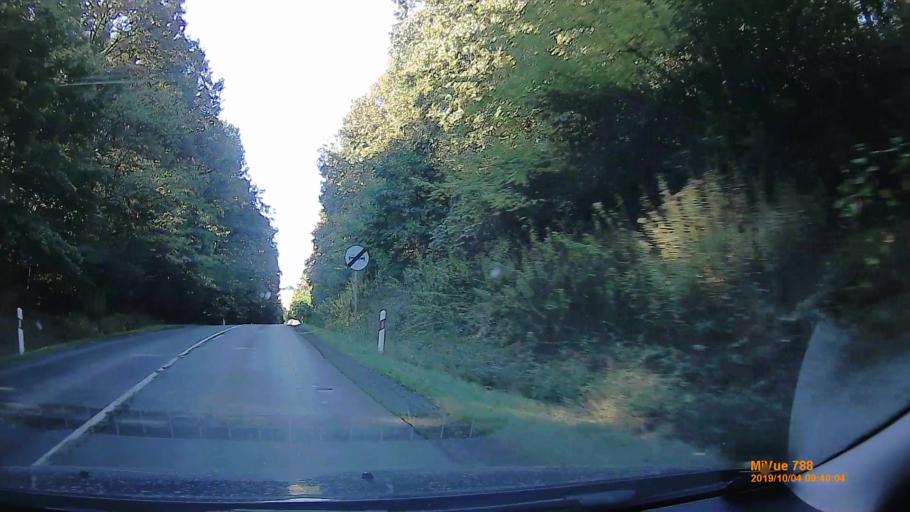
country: HU
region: Somogy
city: Kaposvar
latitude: 46.4438
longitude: 17.8000
